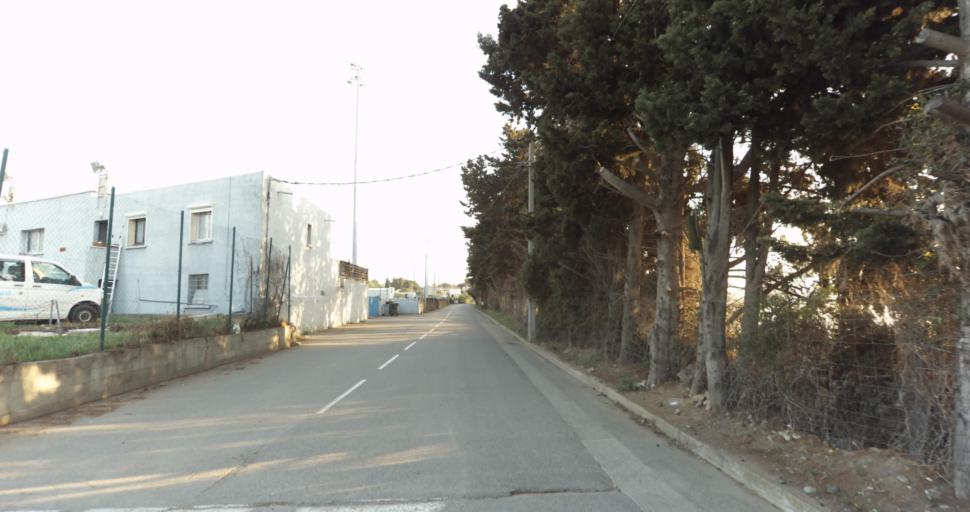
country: FR
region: Corsica
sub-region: Departement de la Haute-Corse
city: Biguglia
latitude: 42.6196
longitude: 9.4433
